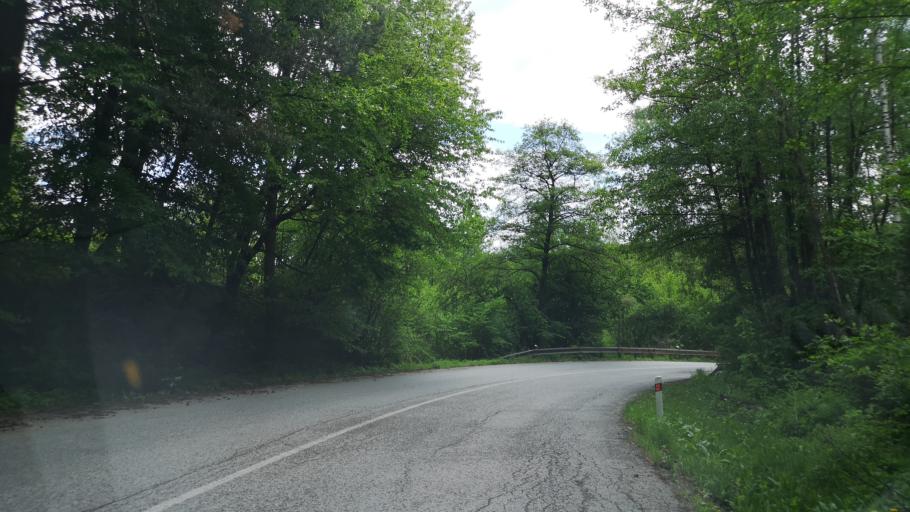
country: SK
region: Kosicky
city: Dobsina
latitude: 48.6486
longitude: 20.3012
